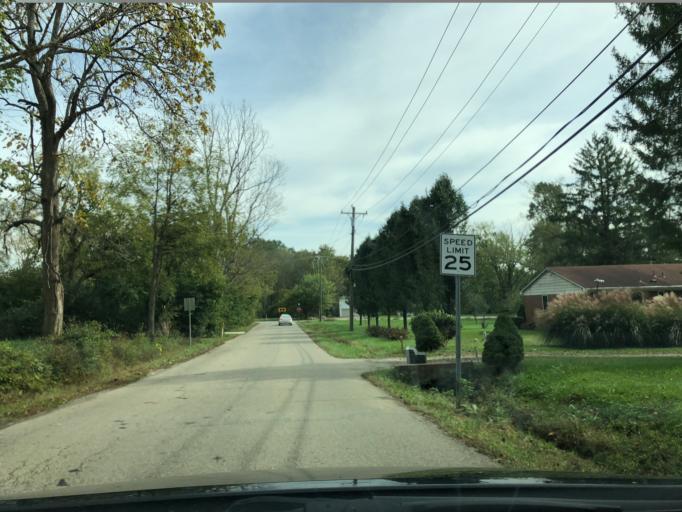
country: US
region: Ohio
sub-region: Hamilton County
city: The Village of Indian Hill
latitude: 39.2158
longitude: -84.3001
